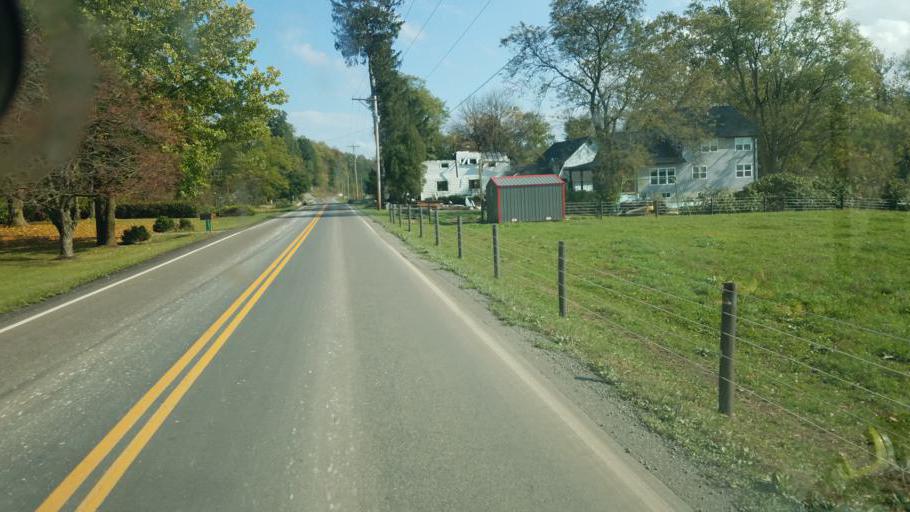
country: US
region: Ohio
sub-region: Holmes County
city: Millersburg
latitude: 40.6156
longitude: -81.8701
